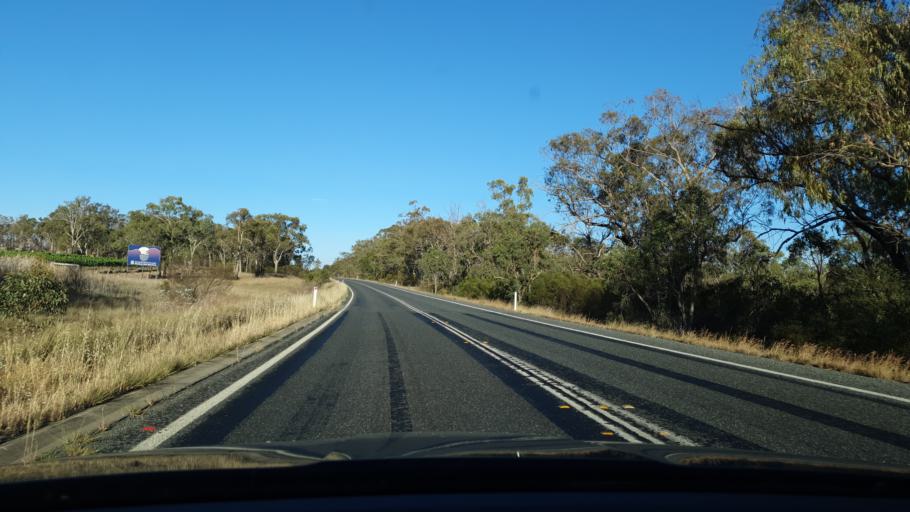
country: AU
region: Queensland
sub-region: Southern Downs
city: Stanthorpe
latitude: -28.6431
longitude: 151.9343
